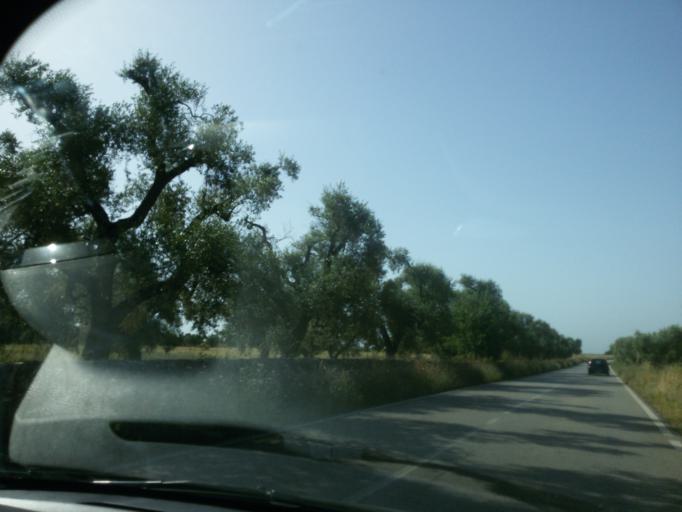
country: IT
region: Apulia
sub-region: Provincia di Brindisi
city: Mesagne
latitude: 40.5126
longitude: 17.8267
